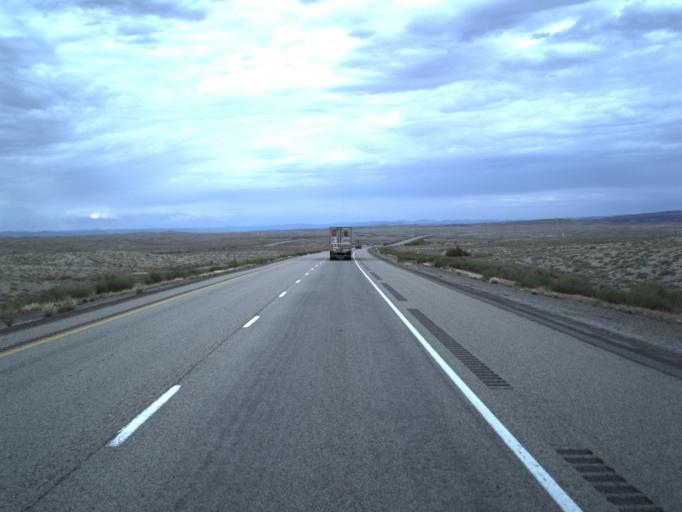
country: US
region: Utah
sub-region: Grand County
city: Moab
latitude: 38.9592
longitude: -109.3810
